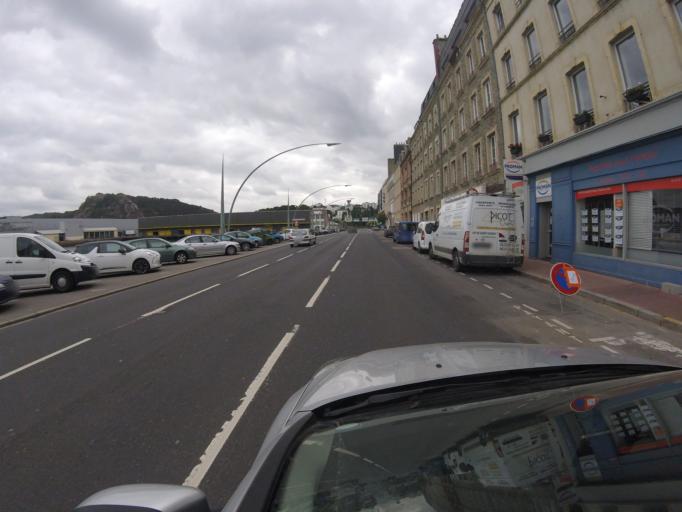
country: FR
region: Lower Normandy
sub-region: Departement de la Manche
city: Cherbourg-Octeville
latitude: 49.6364
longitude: -1.6219
